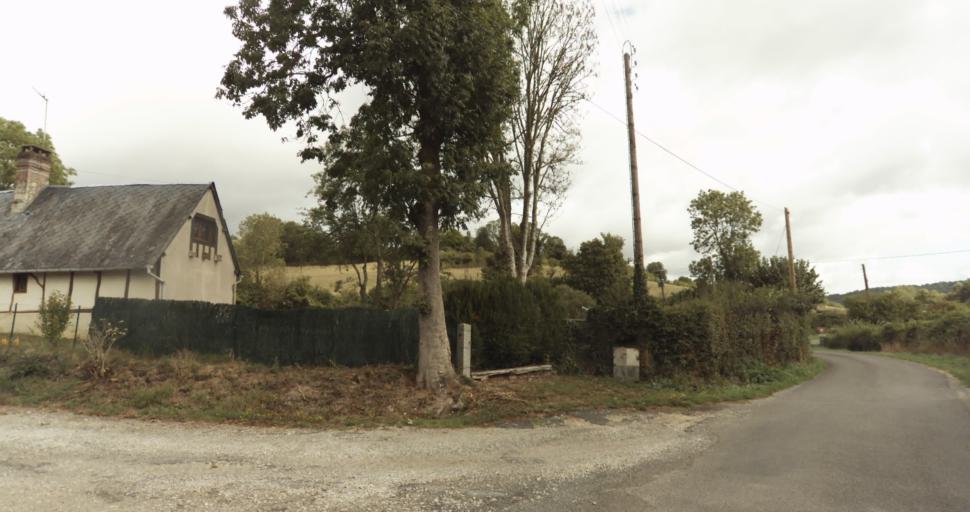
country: FR
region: Lower Normandy
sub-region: Departement de l'Orne
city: Gace
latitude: 48.8403
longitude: 0.2609
